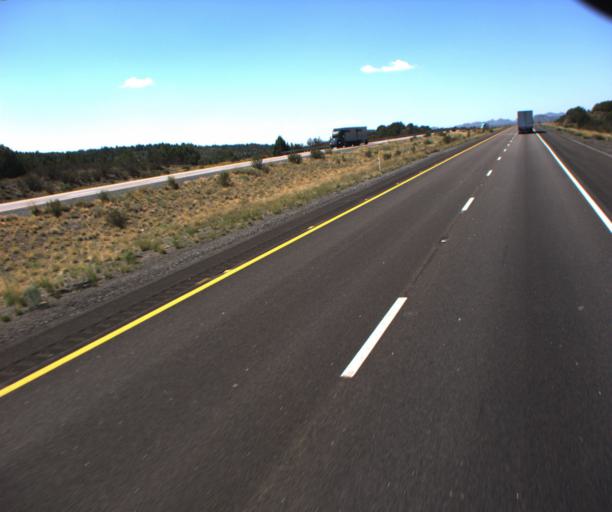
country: US
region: Arizona
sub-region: Mohave County
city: Peach Springs
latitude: 35.1969
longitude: -113.3067
